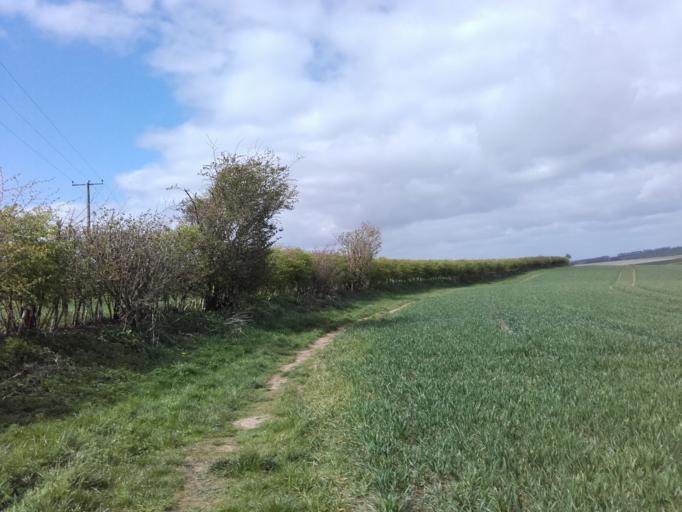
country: GB
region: England
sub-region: East Riding of Yorkshire
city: Market Weighton
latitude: 53.8685
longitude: -0.6179
